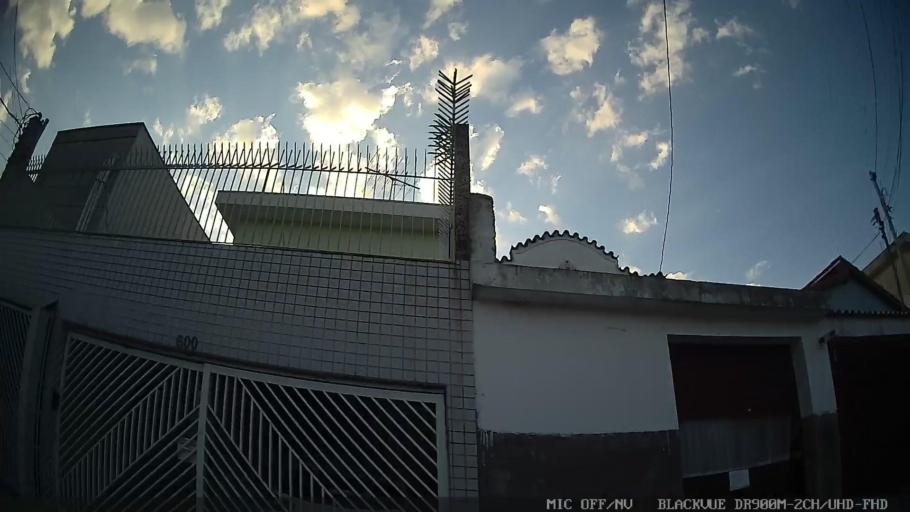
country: BR
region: Sao Paulo
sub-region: Sao Caetano Do Sul
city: Sao Caetano do Sul
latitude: -23.5792
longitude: -46.5576
